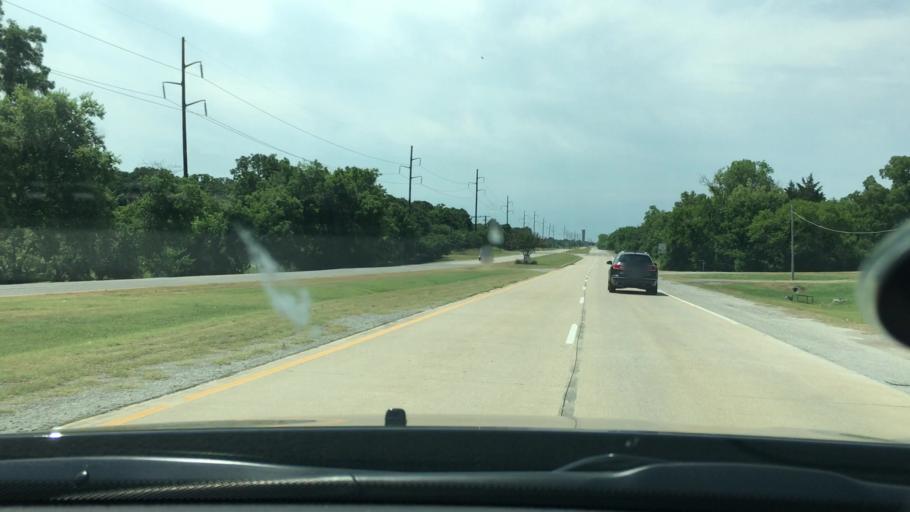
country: US
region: Oklahoma
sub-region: Carter County
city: Ardmore
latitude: 34.2193
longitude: -97.1433
